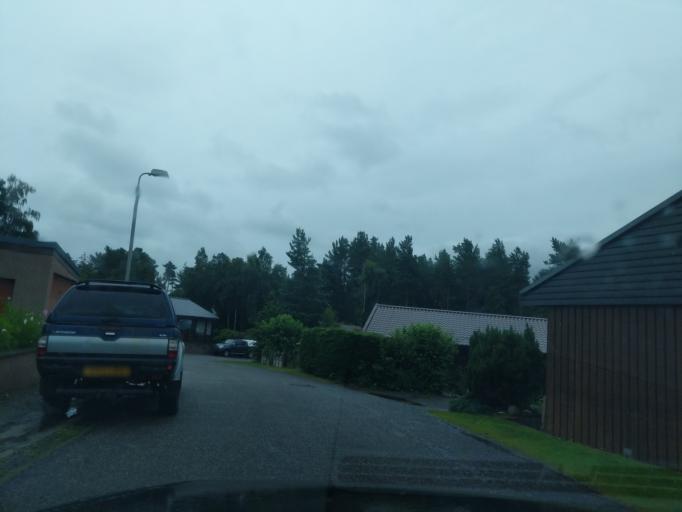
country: GB
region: Scotland
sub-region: Aberdeenshire
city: Aboyne
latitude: 57.0722
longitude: -2.7951
